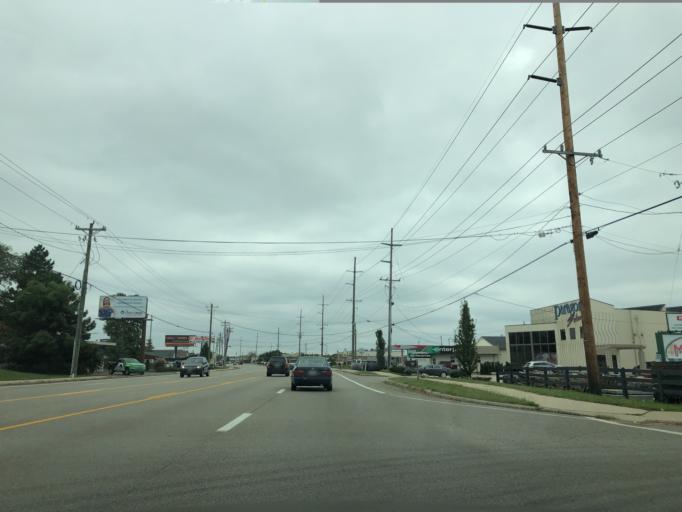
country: US
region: Ohio
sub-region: Hamilton County
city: Sixteen Mile Stand
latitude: 39.2882
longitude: -84.3034
